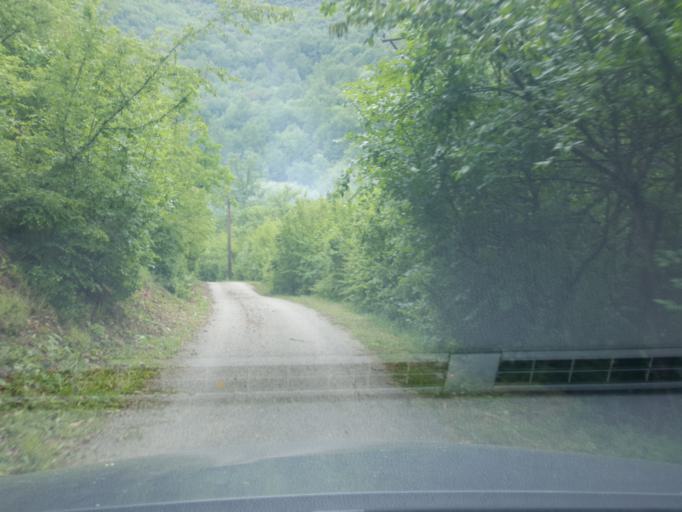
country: RS
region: Central Serbia
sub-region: Zajecarski Okrug
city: Soko Banja
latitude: 43.6312
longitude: 21.9916
